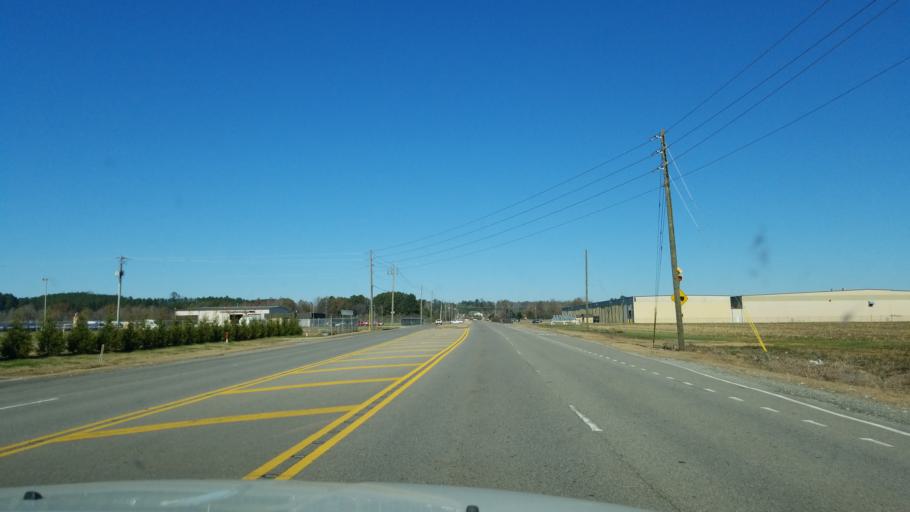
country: US
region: Alabama
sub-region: Tuscaloosa County
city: Northport
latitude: 33.2265
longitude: -87.6400
